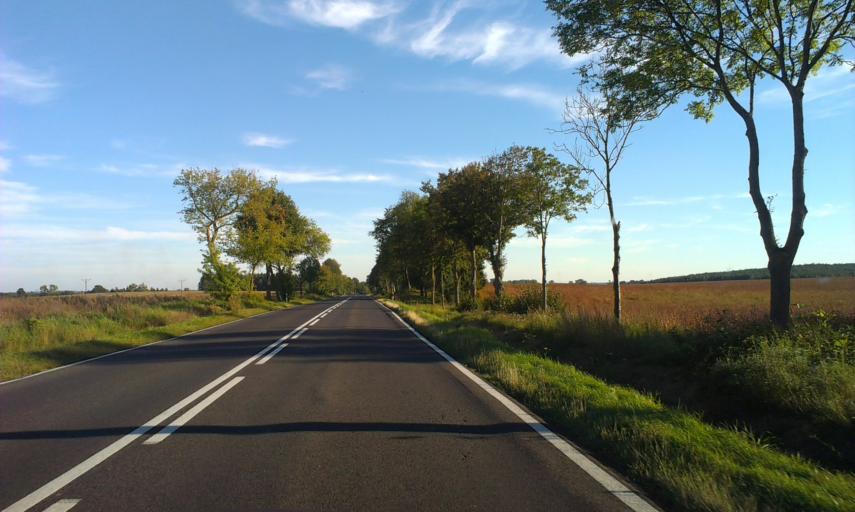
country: PL
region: West Pomeranian Voivodeship
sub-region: Powiat szczecinecki
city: Szczecinek
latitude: 53.7721
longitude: 16.6440
